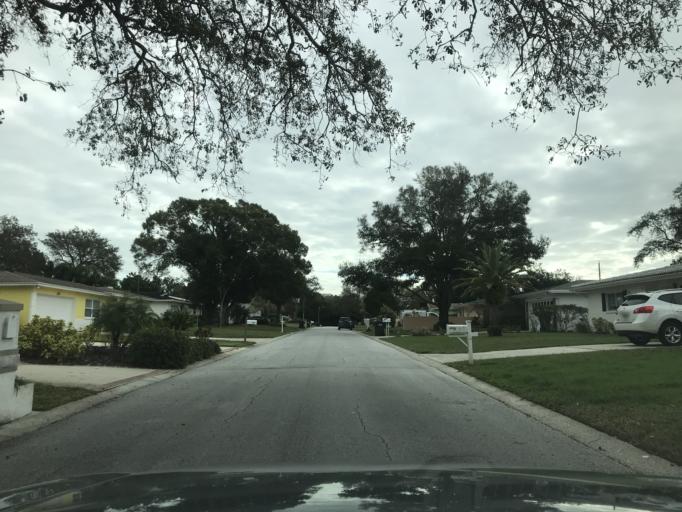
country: US
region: Florida
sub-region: Pinellas County
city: Largo
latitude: 27.9348
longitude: -82.7780
